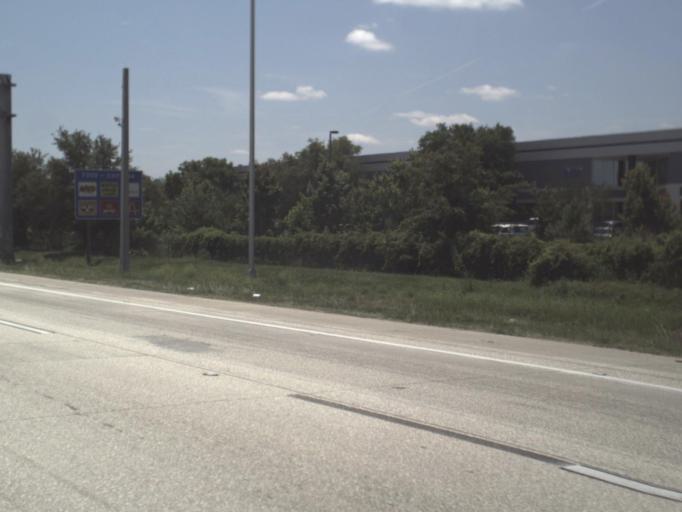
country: US
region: Florida
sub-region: Duval County
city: Jacksonville
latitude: 30.2554
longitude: -81.6008
